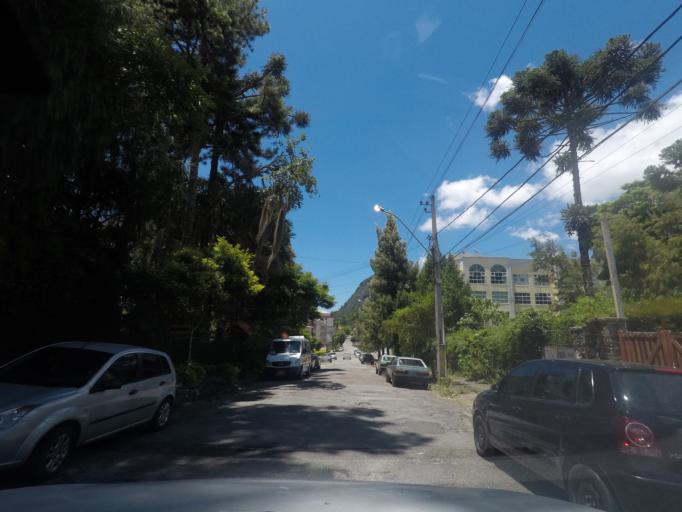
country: BR
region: Rio de Janeiro
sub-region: Teresopolis
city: Teresopolis
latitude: -22.4364
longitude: -42.9801
